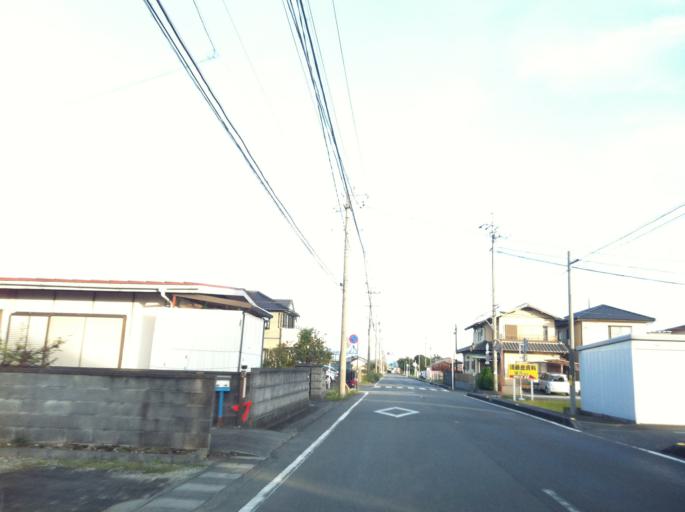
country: JP
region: Shizuoka
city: Fujieda
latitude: 34.8396
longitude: 138.2900
